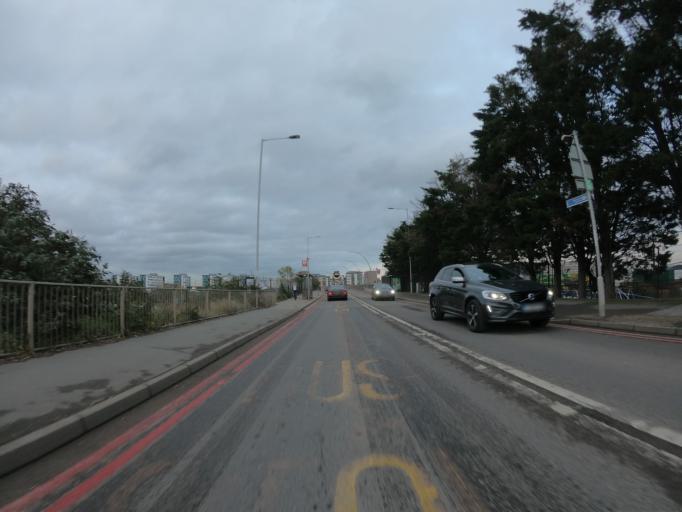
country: GB
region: England
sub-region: Greater London
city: Woolwich
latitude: 51.5036
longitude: 0.0707
